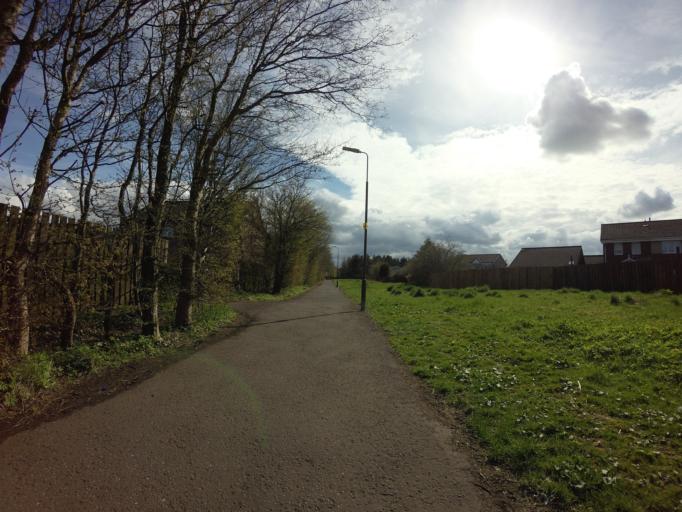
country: GB
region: Scotland
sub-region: West Lothian
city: Livingston
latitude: 55.8988
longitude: -3.5395
